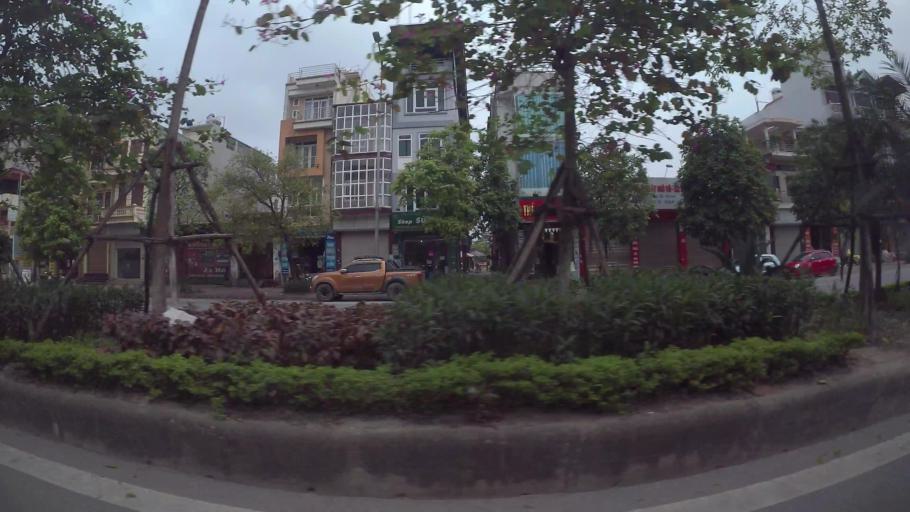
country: VN
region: Ha Noi
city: Trau Quy
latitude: 21.0710
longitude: 105.9032
